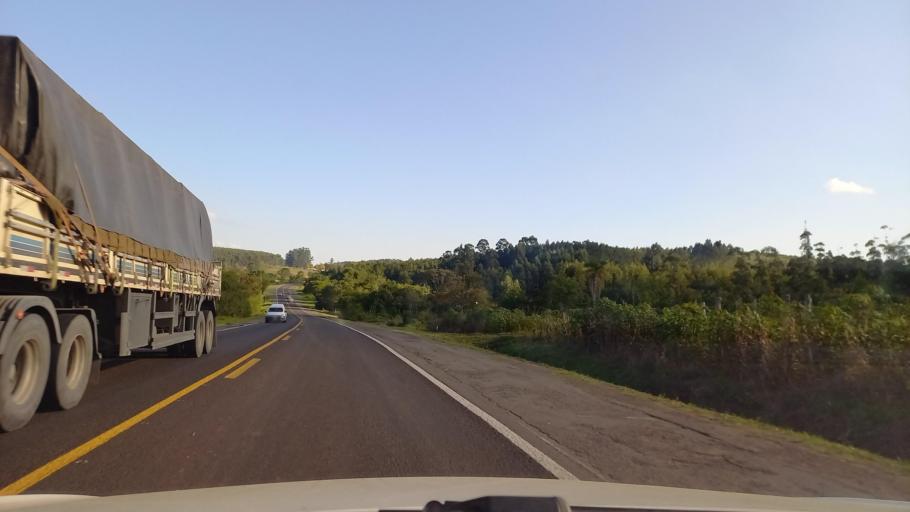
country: BR
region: Rio Grande do Sul
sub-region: Taquari
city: Taquari
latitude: -29.6993
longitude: -51.7512
